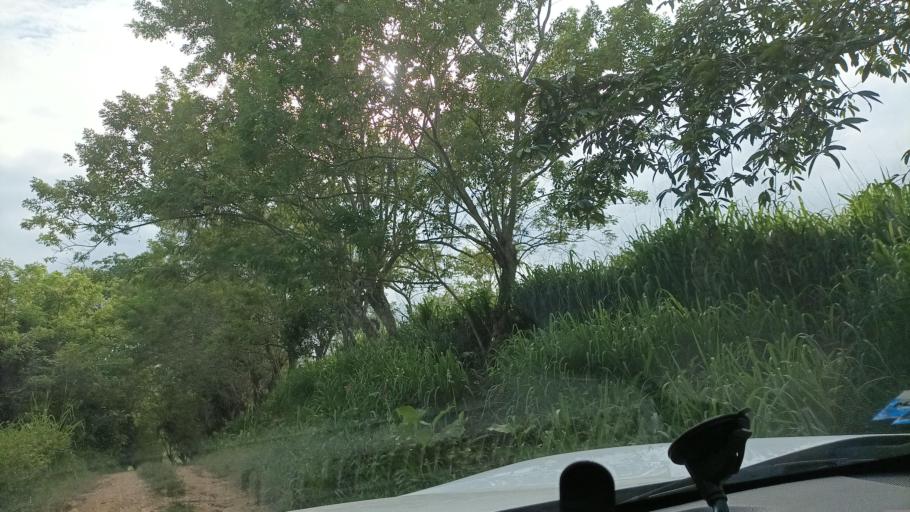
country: MX
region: Veracruz
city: Soconusco
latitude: 17.9503
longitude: -94.8813
